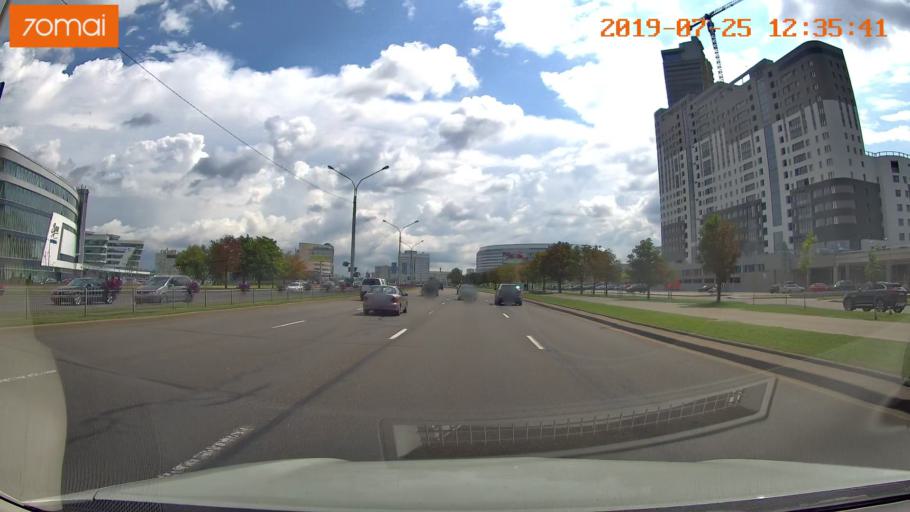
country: BY
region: Minsk
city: Zhdanovichy
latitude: 53.9387
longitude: 27.4743
